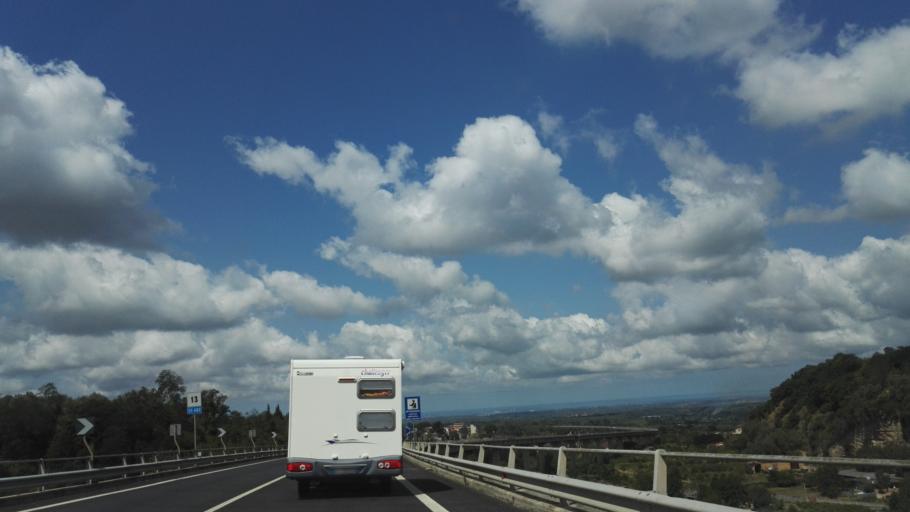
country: IT
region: Calabria
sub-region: Provincia di Reggio Calabria
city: Anoia Superiore
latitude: 38.4167
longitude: 16.1087
